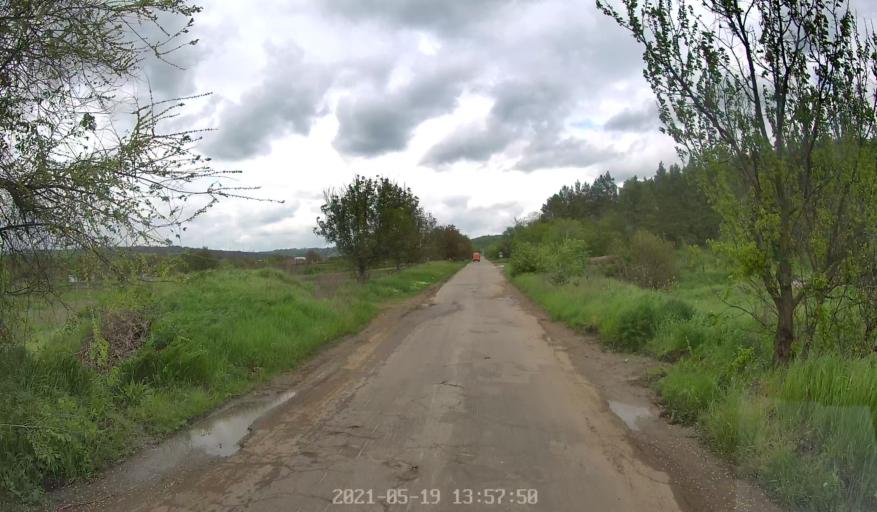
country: MD
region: Chisinau
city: Chisinau
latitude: 47.0403
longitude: 28.9104
